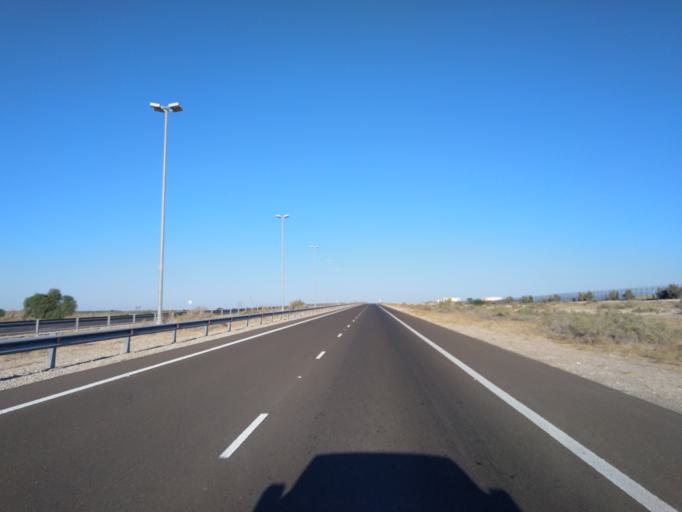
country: OM
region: Al Buraimi
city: Al Buraymi
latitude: 24.5348
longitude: 55.5838
